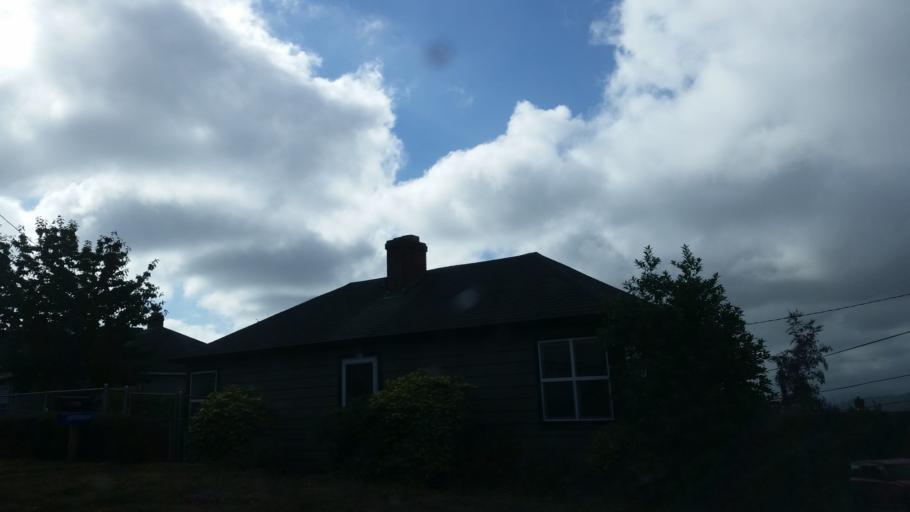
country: US
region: Oregon
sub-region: Clatsop County
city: Astoria
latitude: 46.1814
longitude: -123.8542
